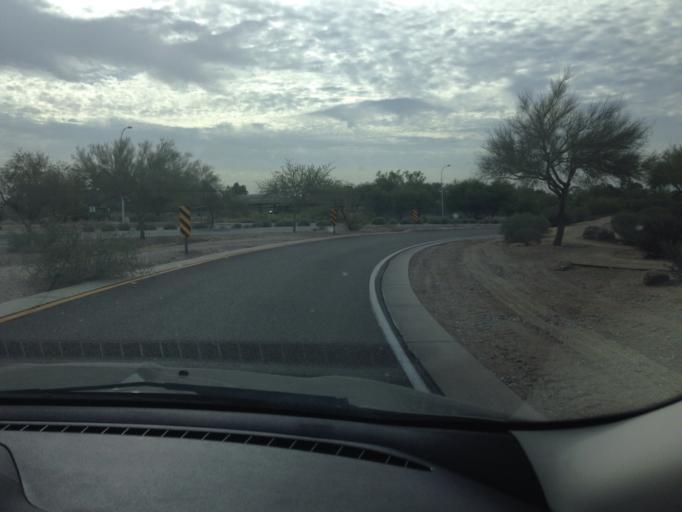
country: US
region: Arizona
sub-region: Maricopa County
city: Paradise Valley
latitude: 33.5313
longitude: -112.0270
